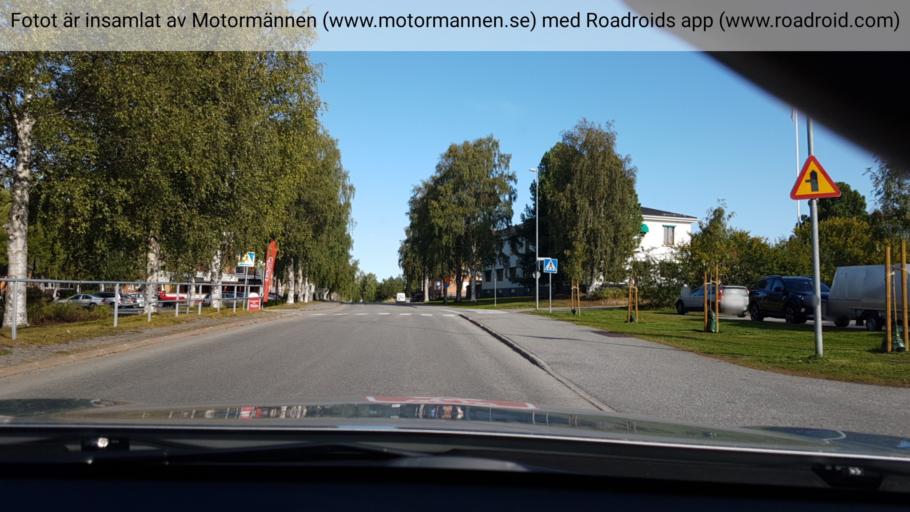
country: SE
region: Vaesterbotten
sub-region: Lycksele Kommun
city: Lycksele
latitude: 64.5942
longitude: 18.6705
